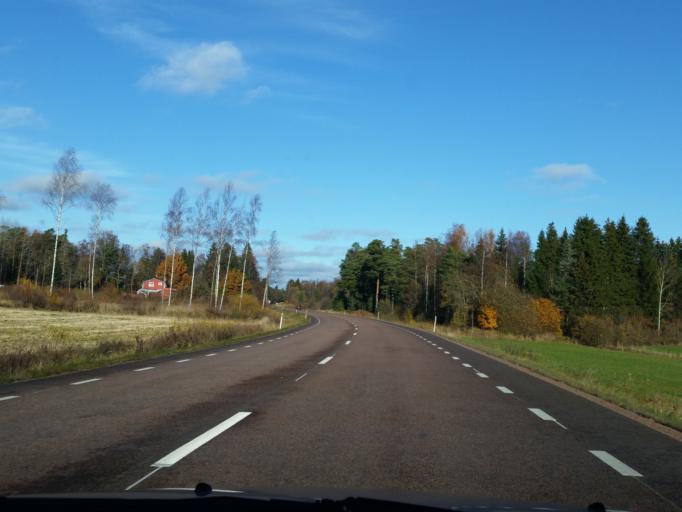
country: AX
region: Alands landsbygd
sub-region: Finstroem
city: Finstroem
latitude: 60.2180
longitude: 19.9818
